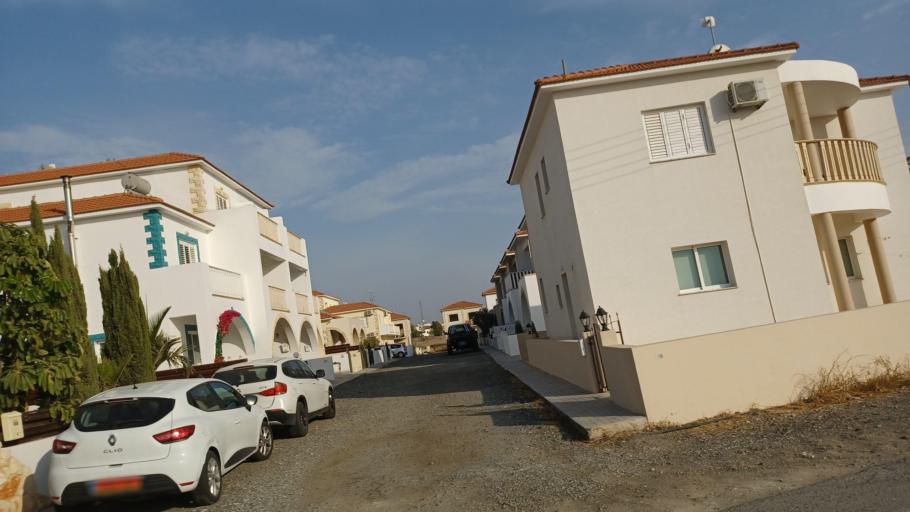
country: CY
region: Ammochostos
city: Acheritou
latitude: 35.0766
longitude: 33.8739
